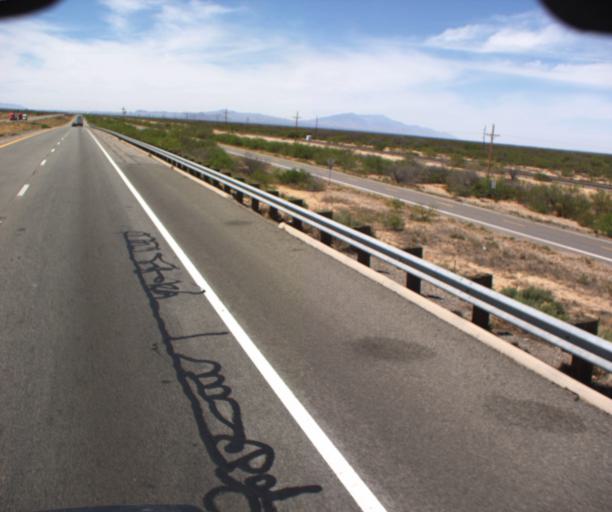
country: US
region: Arizona
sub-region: Cochise County
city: Willcox
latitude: 32.2973
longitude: -109.3530
